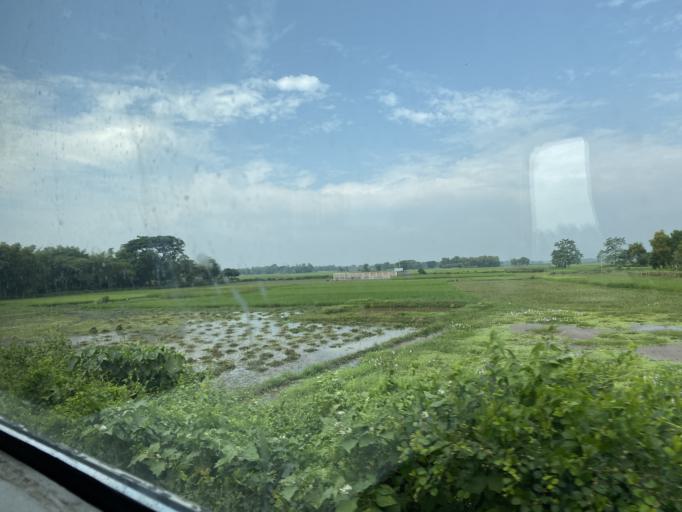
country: IN
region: Tripura
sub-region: West Tripura
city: Agartala
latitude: 23.9967
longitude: 91.2890
